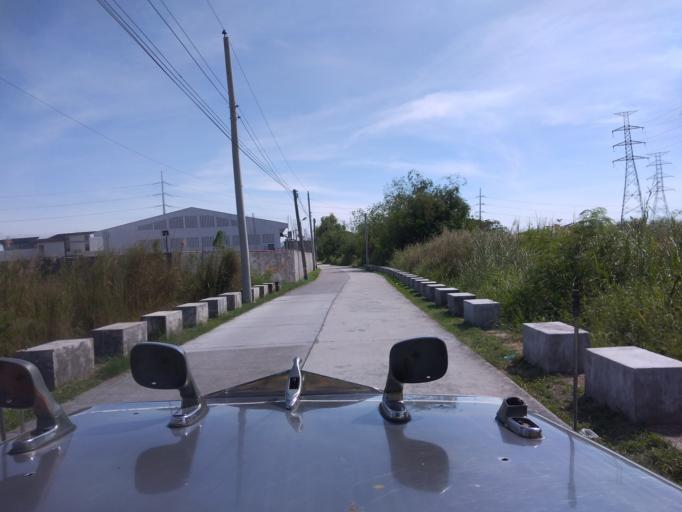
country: PH
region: Central Luzon
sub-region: Province of Pampanga
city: San Juan
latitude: 15.0226
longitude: 120.6676
